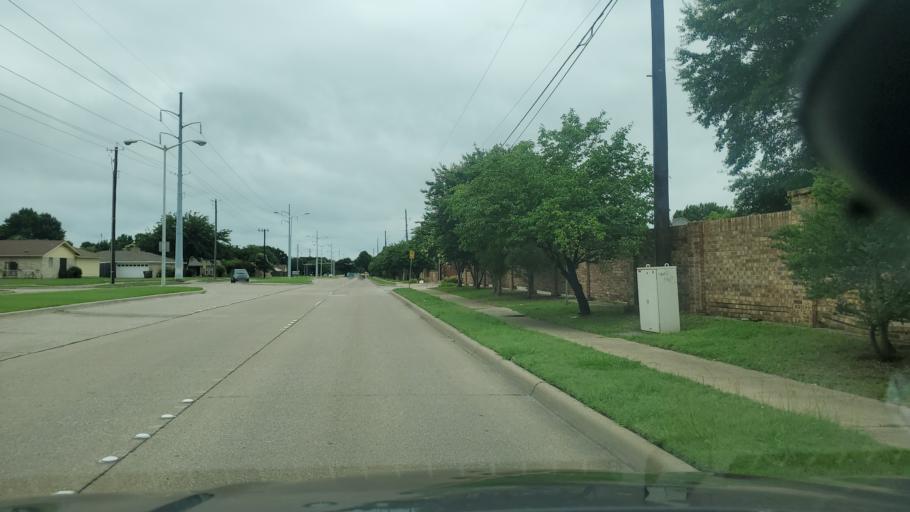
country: US
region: Texas
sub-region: Dallas County
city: Garland
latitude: 32.9419
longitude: -96.6653
